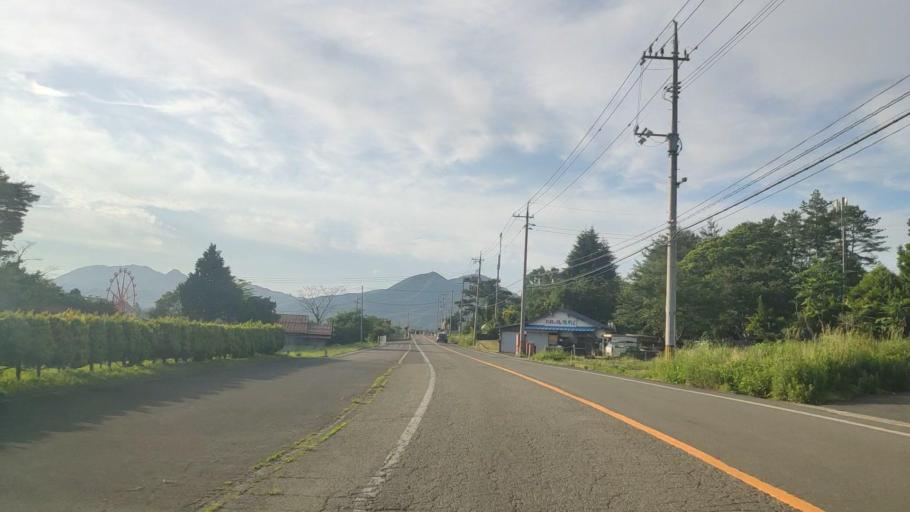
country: JP
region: Tottori
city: Kurayoshi
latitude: 35.2873
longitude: 133.6375
